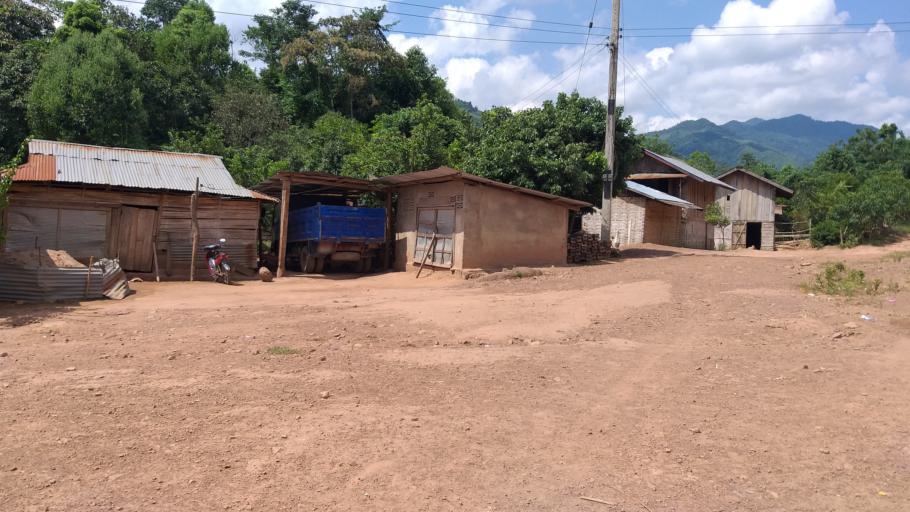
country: LA
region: Phongsali
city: Khoa
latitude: 21.3683
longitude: 102.5326
